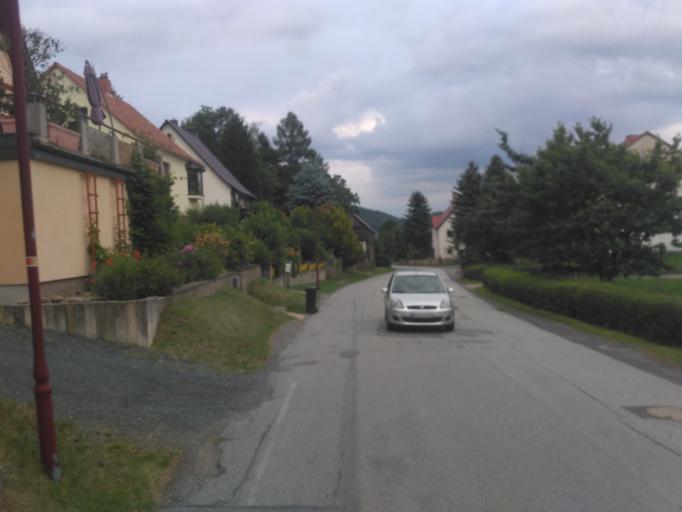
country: DE
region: Saxony
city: Kurort Gohrisch
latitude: 50.8973
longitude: 14.1235
